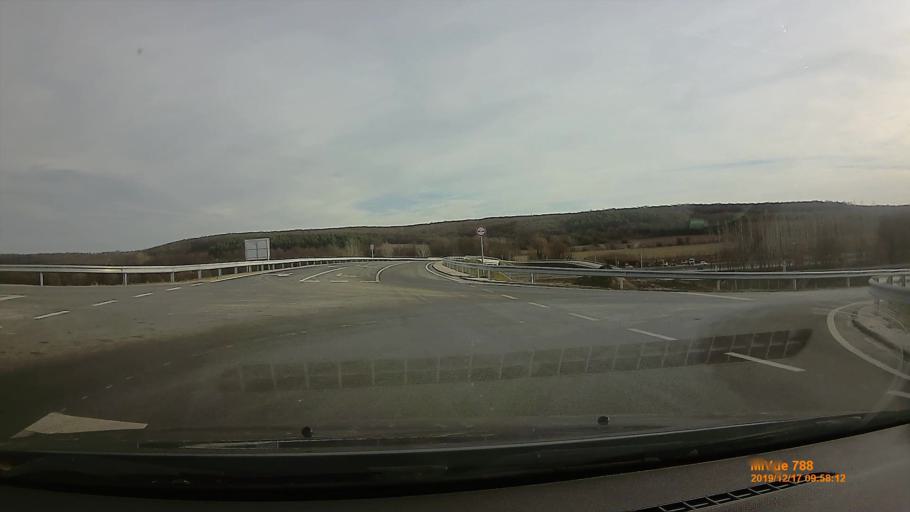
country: HU
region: Somogy
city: Karad
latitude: 46.6235
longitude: 17.7928
